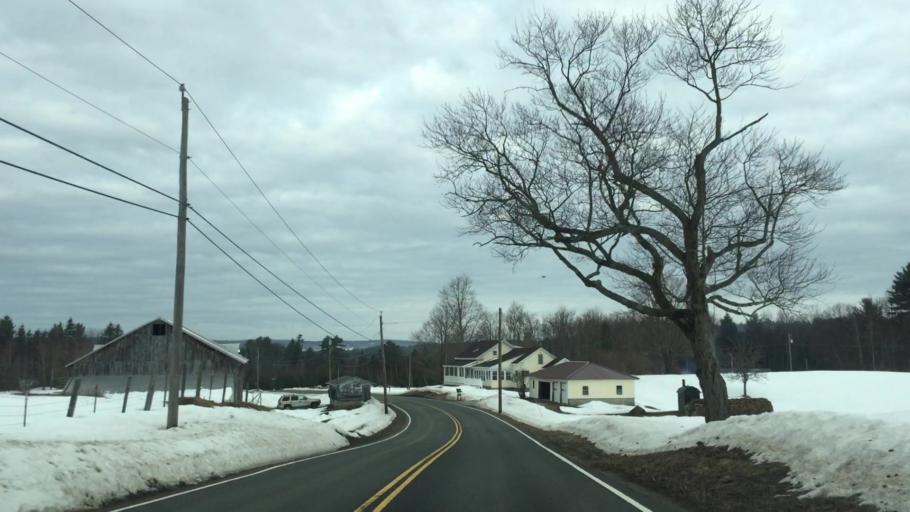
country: US
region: Massachusetts
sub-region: Berkshire County
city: Hinsdale
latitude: 42.4217
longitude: -73.0764
